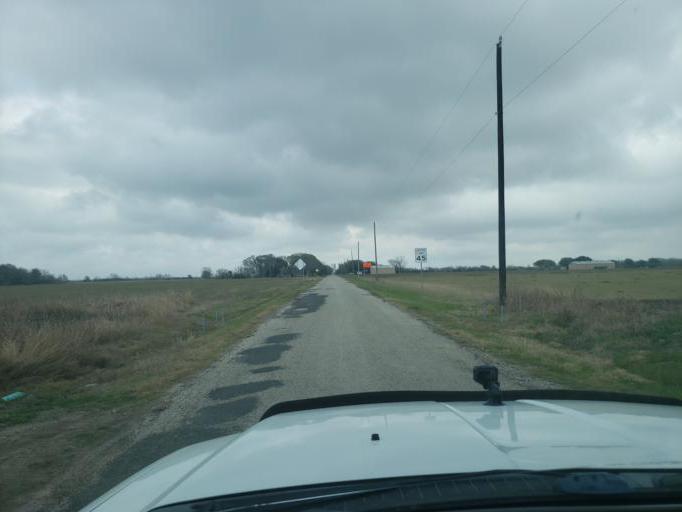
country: US
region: Texas
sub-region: Fort Bend County
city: Needville
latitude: 29.3395
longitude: -95.7654
